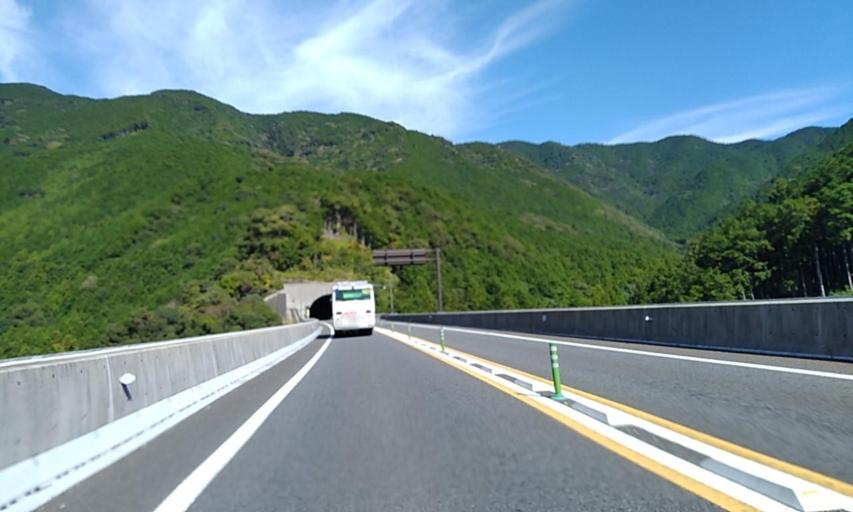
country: JP
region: Mie
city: Owase
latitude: 33.9438
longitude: 136.1539
